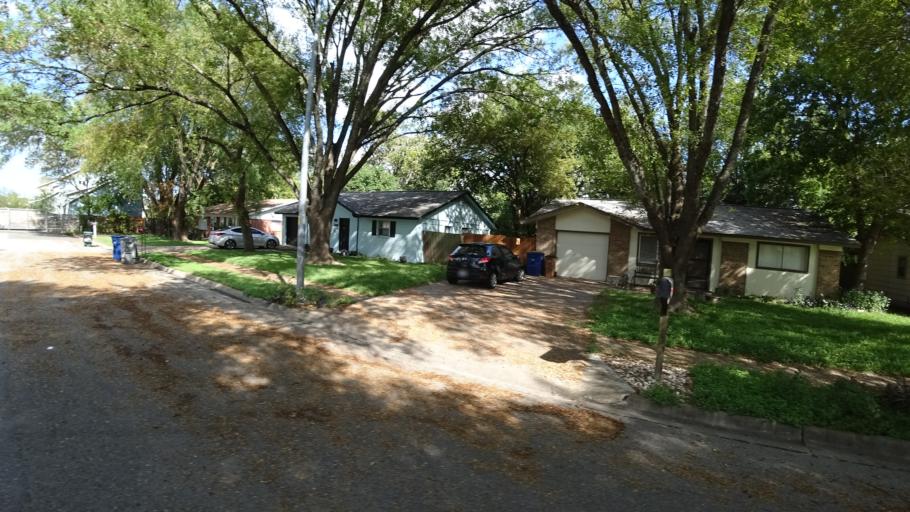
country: US
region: Texas
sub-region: Travis County
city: Onion Creek
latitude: 30.2057
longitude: -97.7842
